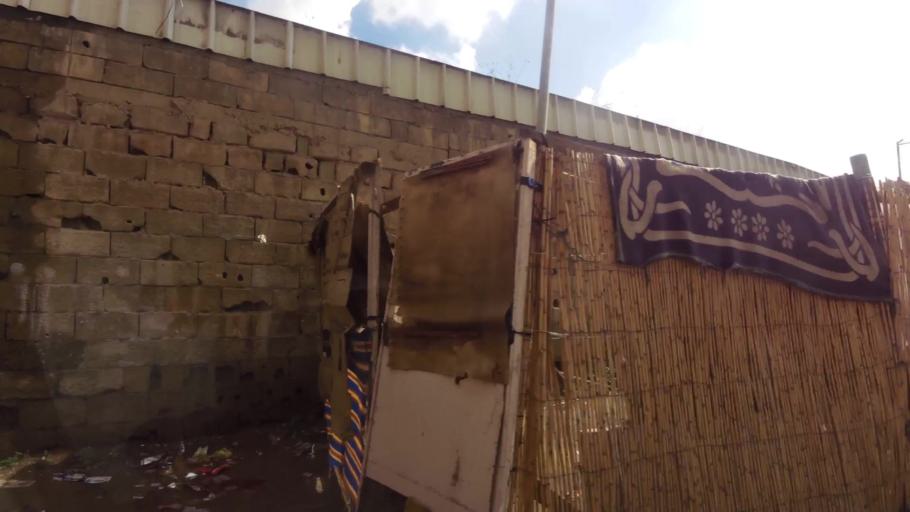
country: MA
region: Grand Casablanca
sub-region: Casablanca
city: Casablanca
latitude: 33.5316
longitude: -7.6690
